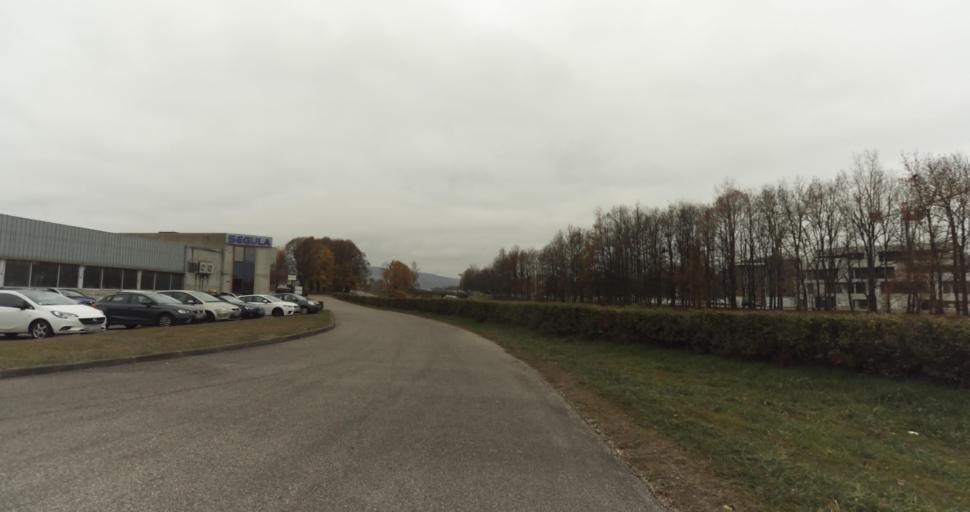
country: FR
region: Rhone-Alpes
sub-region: Departement de la Haute-Savoie
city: Meythet
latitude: 45.9179
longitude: 6.0816
